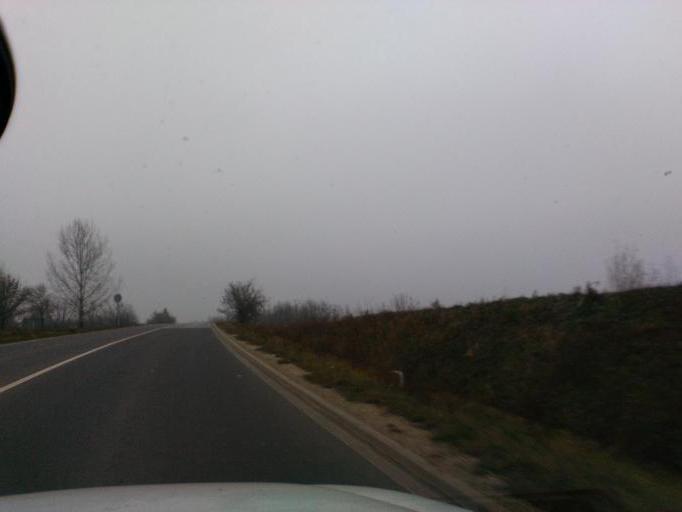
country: HU
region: Pest
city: Soskut
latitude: 47.3762
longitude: 18.8105
